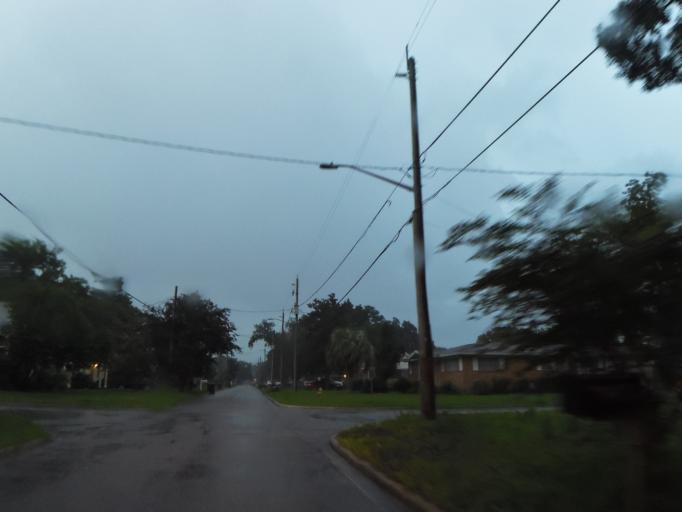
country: US
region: Florida
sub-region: Duval County
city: Jacksonville
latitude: 30.3138
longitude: -81.7289
